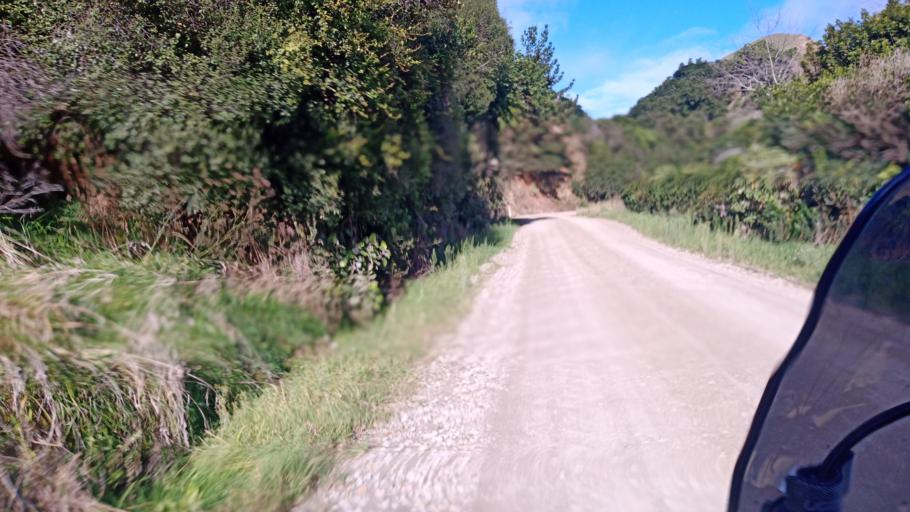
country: NZ
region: Gisborne
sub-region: Gisborne District
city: Gisborne
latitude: -38.5435
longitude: 177.5074
